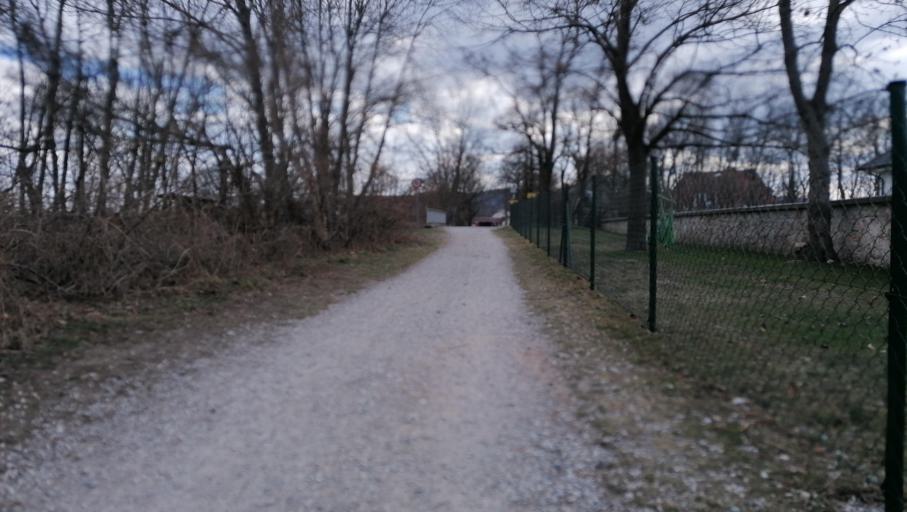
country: AT
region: Lower Austria
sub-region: Wiener Neustadt Stadt
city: Wiener Neustadt
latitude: 47.7969
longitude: 16.2436
